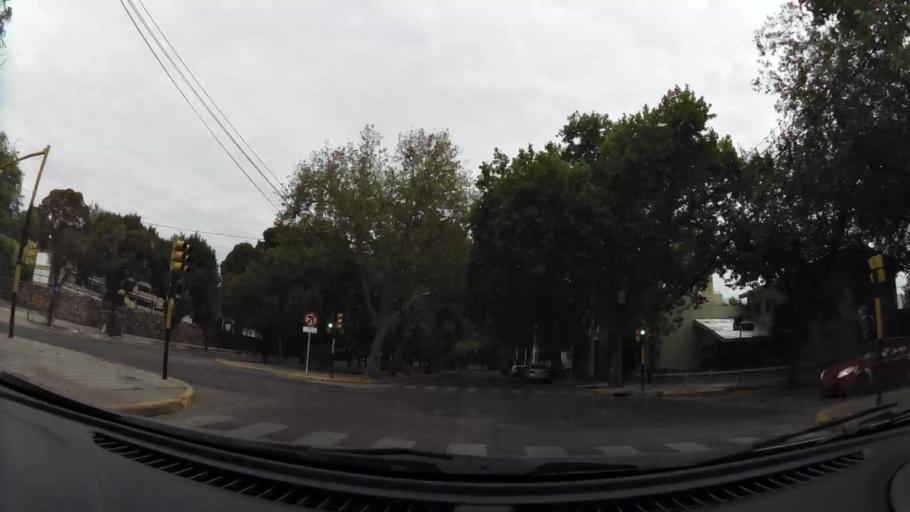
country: AR
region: Mendoza
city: Mendoza
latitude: -32.8961
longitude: -68.8489
